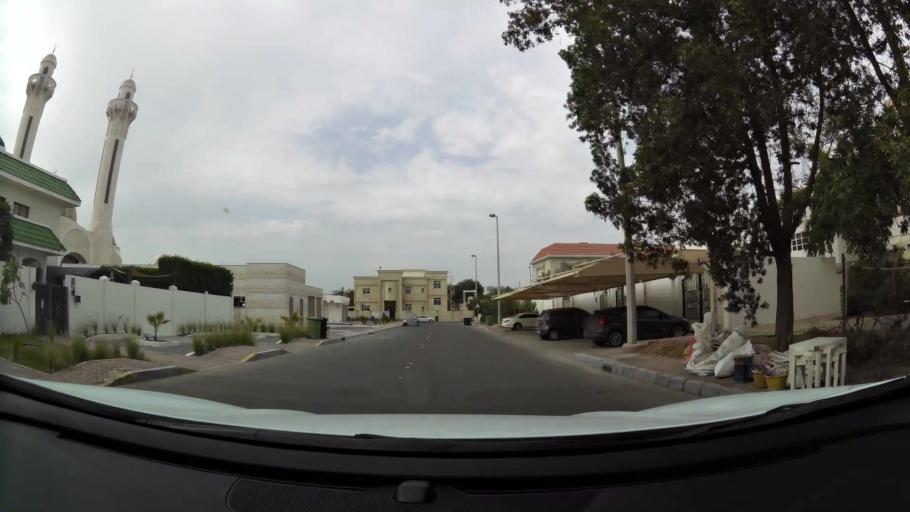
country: AE
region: Abu Dhabi
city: Abu Dhabi
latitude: 24.4623
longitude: 54.3638
